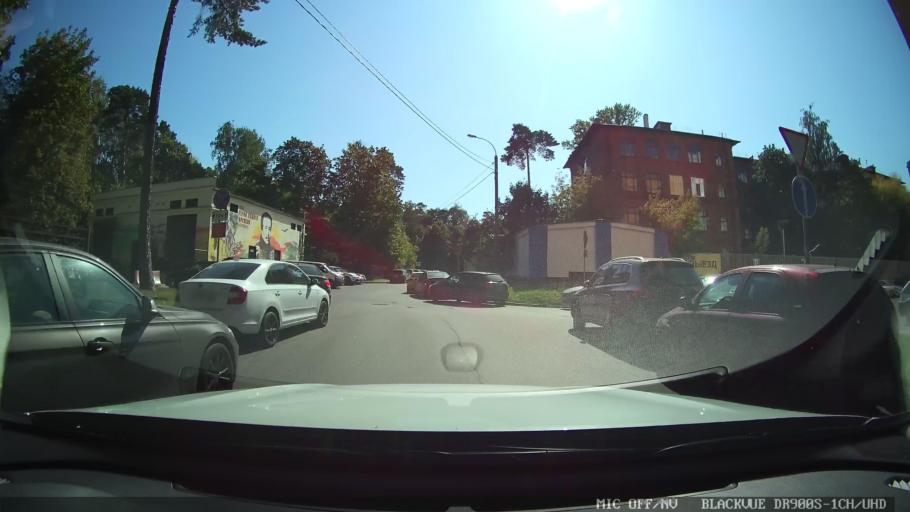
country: RU
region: Moscow
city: Pokrovskoye-Streshnevo
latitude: 55.8093
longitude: 37.4662
